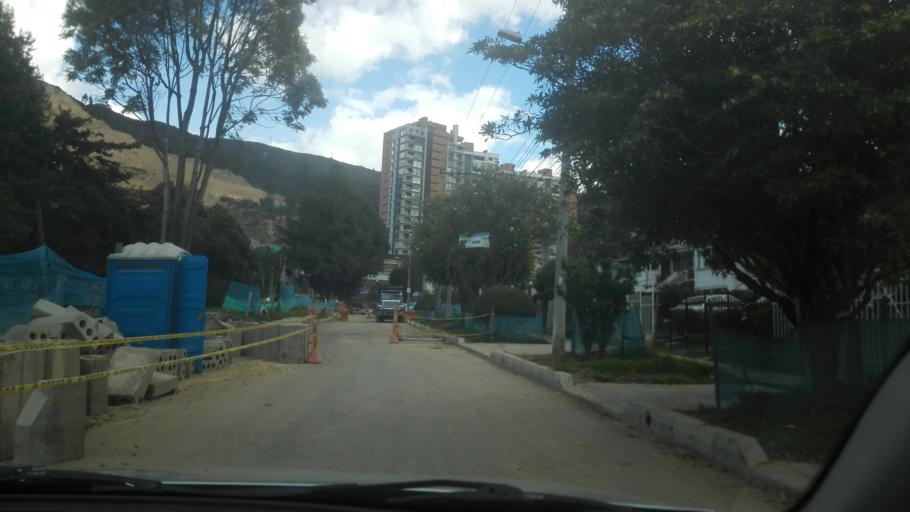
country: CO
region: Cundinamarca
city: La Calera
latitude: 4.7280
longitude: -74.0259
